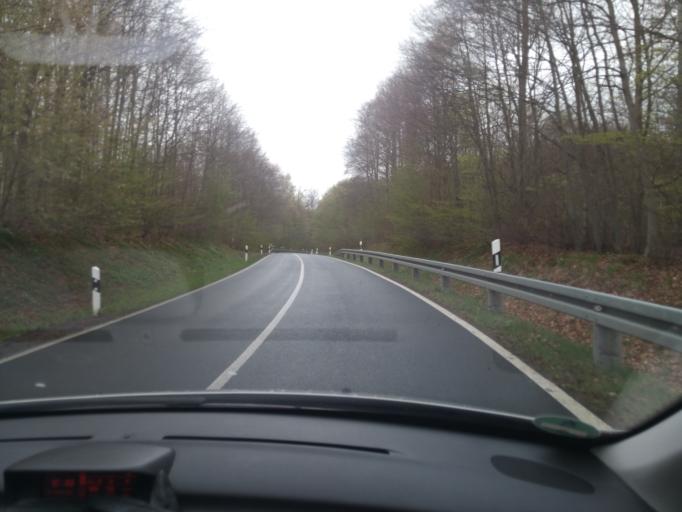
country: DE
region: Mecklenburg-Vorpommern
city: Loitz
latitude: 53.3396
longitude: 13.4145
